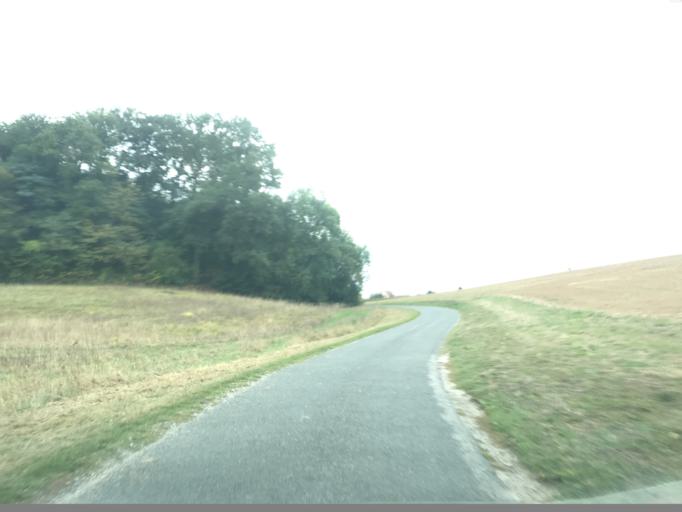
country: FR
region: Haute-Normandie
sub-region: Departement de l'Eure
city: Gravigny
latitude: 49.0831
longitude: 1.2275
